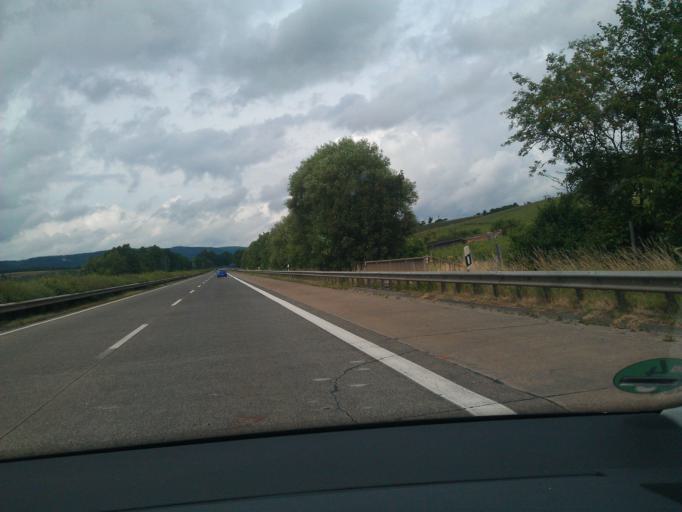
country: DE
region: Rheinland-Pfalz
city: Schweich
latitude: 49.8207
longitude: 6.7589
